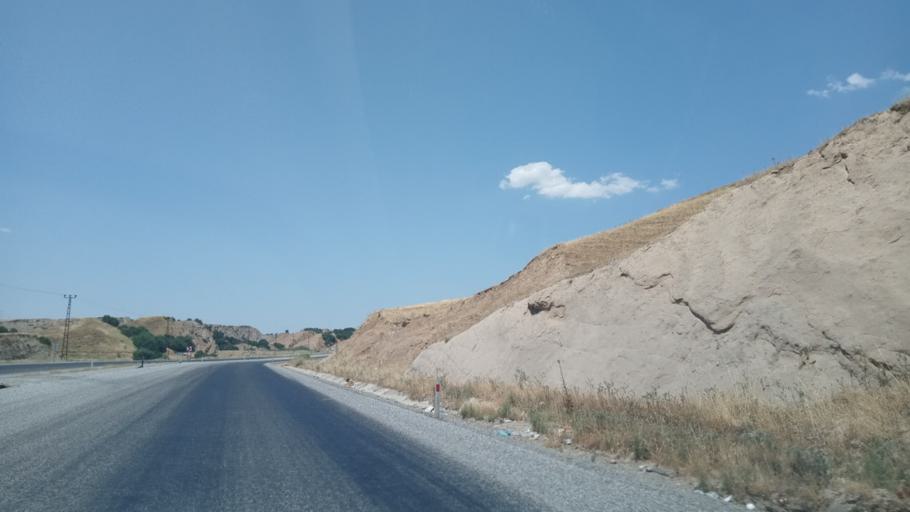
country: TR
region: Batman
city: Kozluk
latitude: 38.1678
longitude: 41.4707
